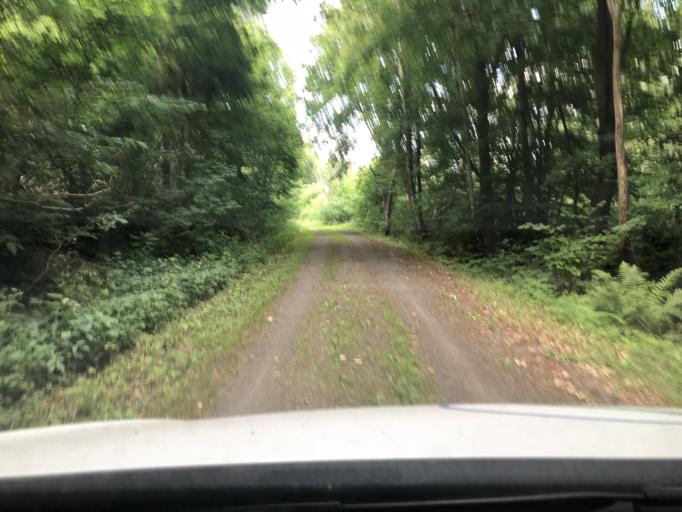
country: SE
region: Skane
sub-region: Kristianstads Kommun
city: Degeberga
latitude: 55.7841
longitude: 14.1733
